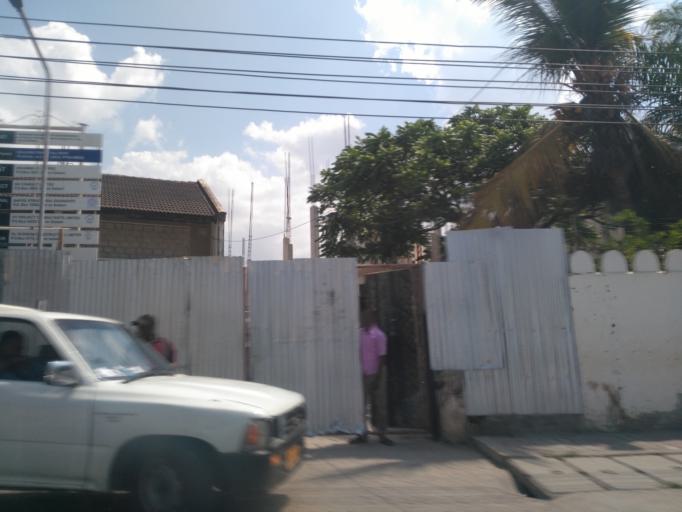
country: TZ
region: Dar es Salaam
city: Dar es Salaam
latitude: -6.8085
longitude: 39.2830
